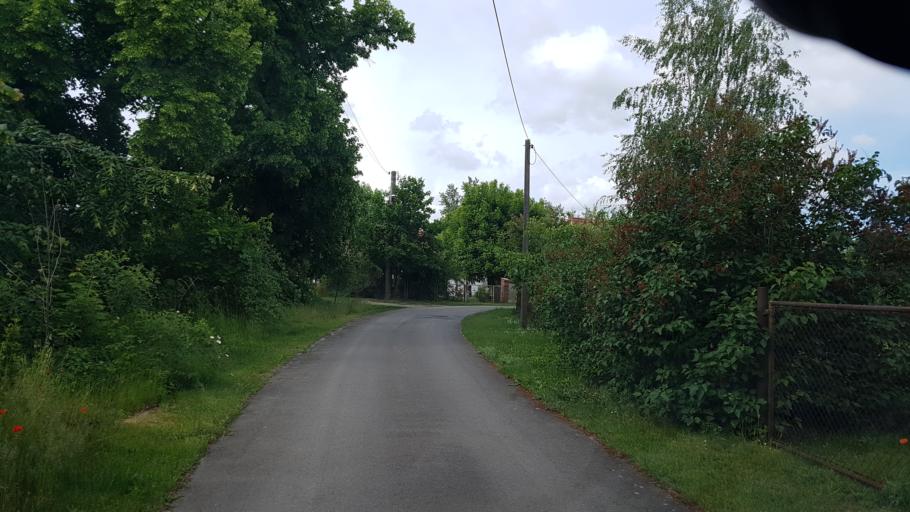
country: DE
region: Brandenburg
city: Crinitz
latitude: 51.8076
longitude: 13.8170
